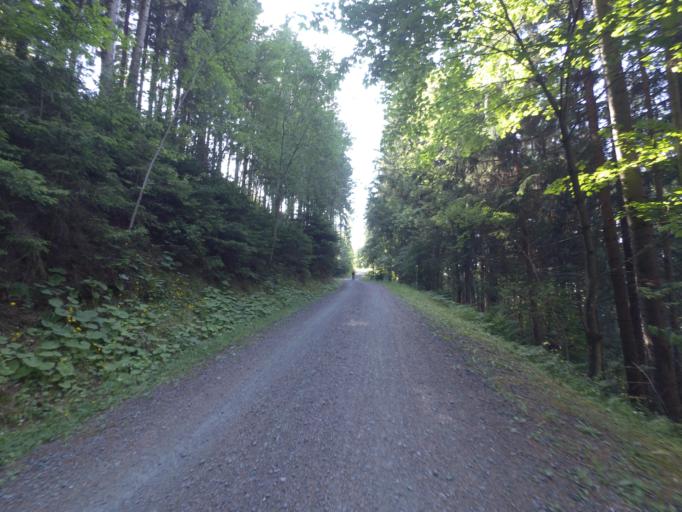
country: AT
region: Carinthia
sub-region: Politischer Bezirk Spittal an der Drau
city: Seeboden
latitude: 46.8059
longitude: 13.5314
